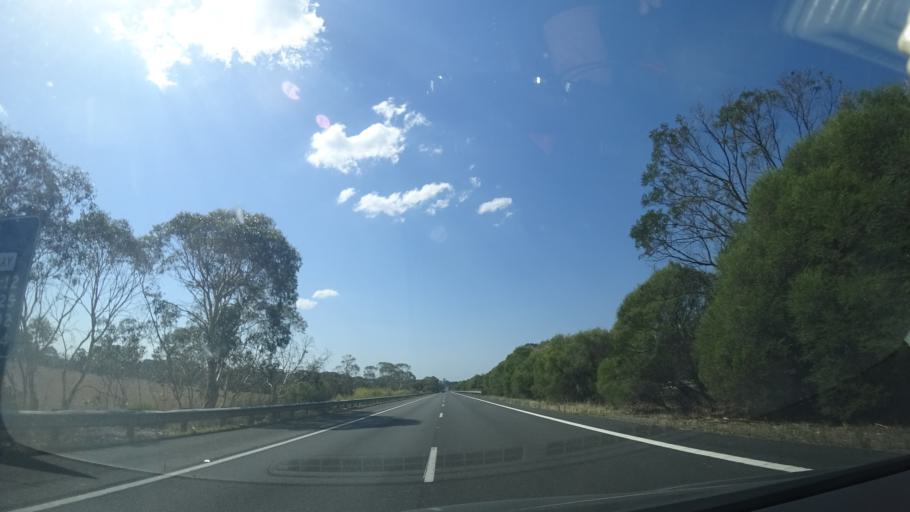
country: AU
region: New South Wales
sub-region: Wingecarribee
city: Bundanoon
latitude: -34.5779
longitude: 150.2527
